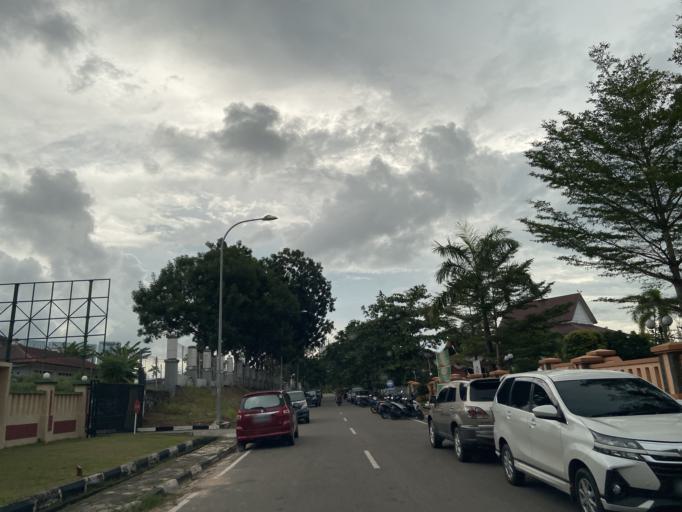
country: SG
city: Singapore
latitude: 1.1258
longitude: 104.0570
